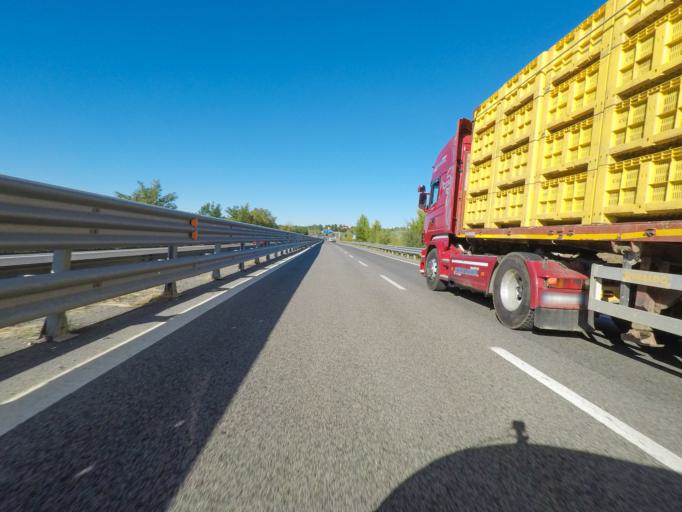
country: IT
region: Tuscany
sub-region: Provincia di Siena
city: Rosia
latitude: 43.2353
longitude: 11.2779
